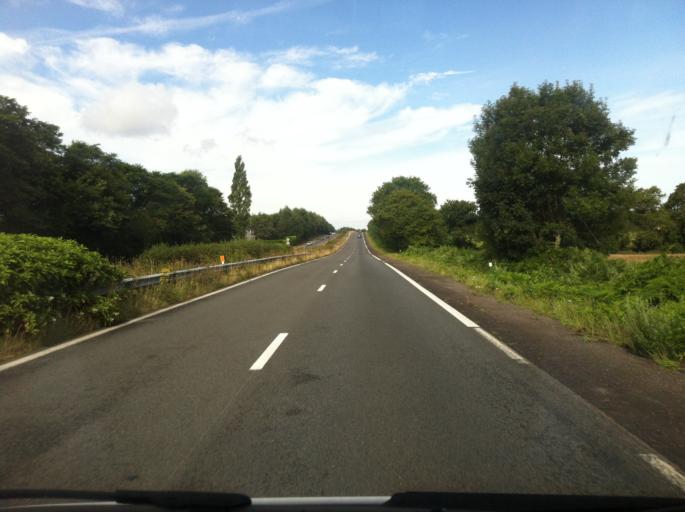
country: FR
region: Brittany
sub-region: Departement des Cotes-d'Armor
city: Graces
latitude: 48.5669
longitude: -3.2278
